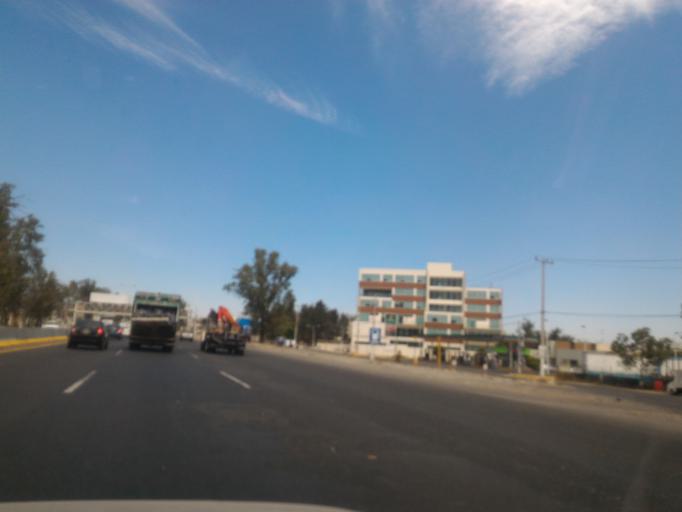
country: MX
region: Jalisco
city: Guadalajara
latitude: 20.6470
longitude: -103.4427
